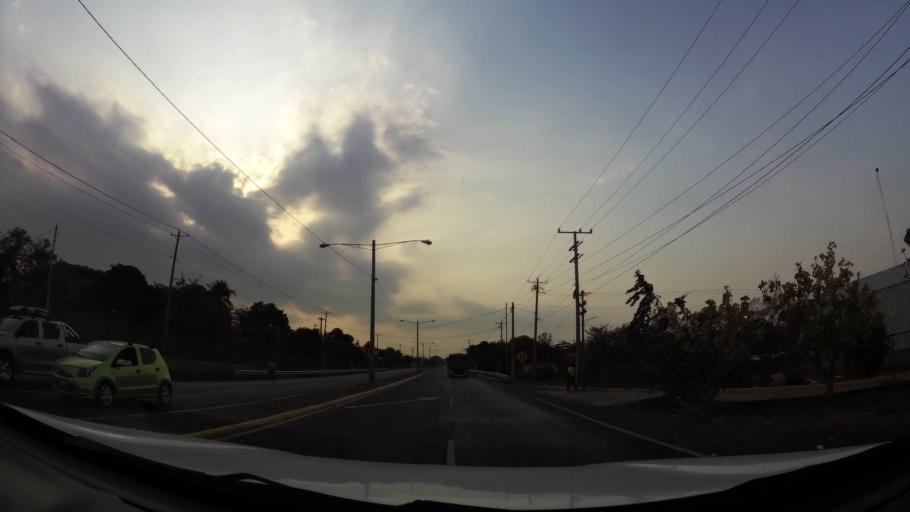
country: NI
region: Managua
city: Ciudad Sandino
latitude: 12.1777
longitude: -86.3521
